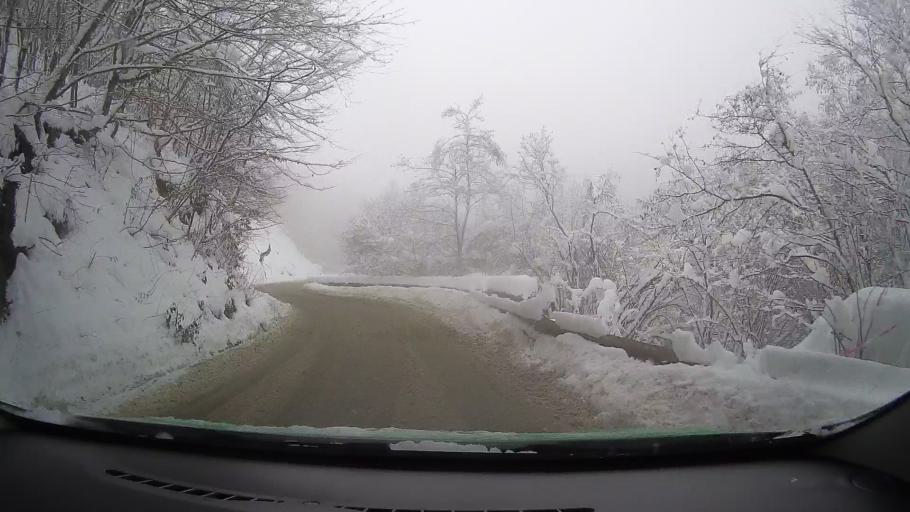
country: RO
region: Sibiu
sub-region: Comuna Tilisca
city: Tilisca
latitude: 45.7992
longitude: 23.7954
